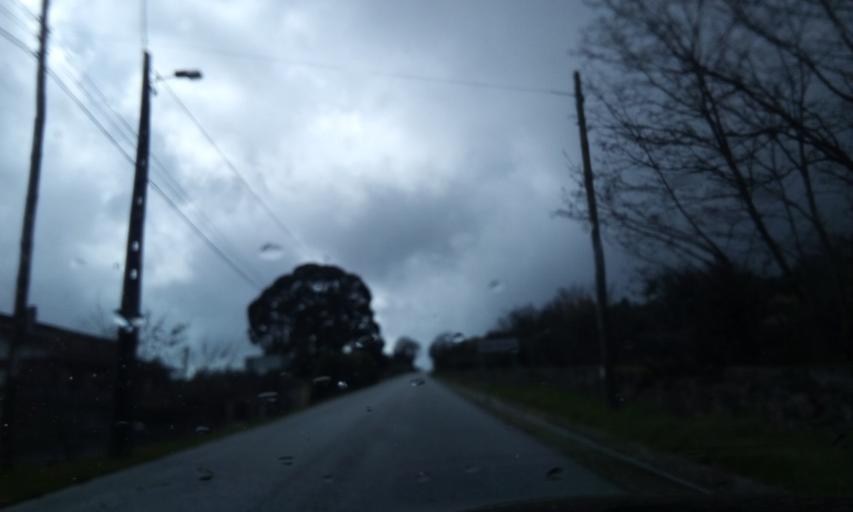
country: PT
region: Guarda
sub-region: Fornos de Algodres
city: Fornos de Algodres
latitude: 40.6222
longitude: -7.6037
